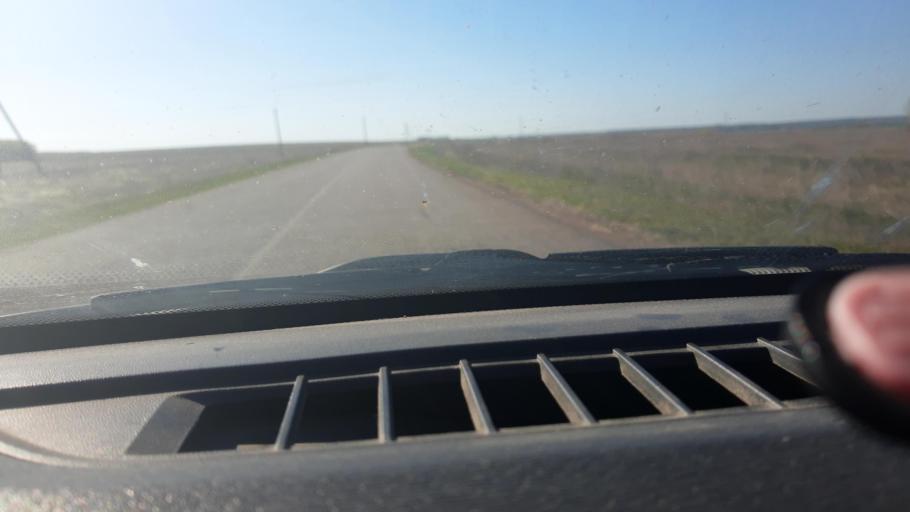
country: RU
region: Bashkortostan
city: Asanovo
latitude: 54.8189
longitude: 55.4760
